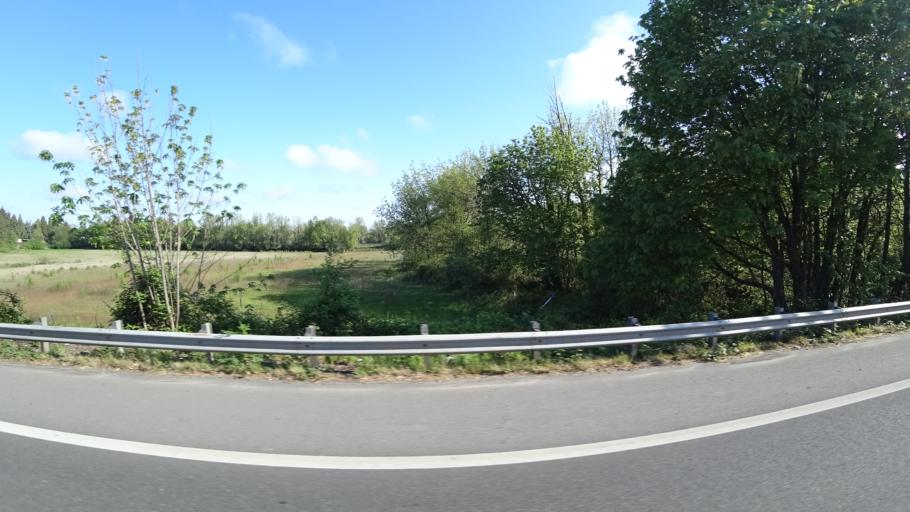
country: US
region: Oregon
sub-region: Washington County
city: Hillsboro
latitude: 45.5201
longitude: -123.0118
